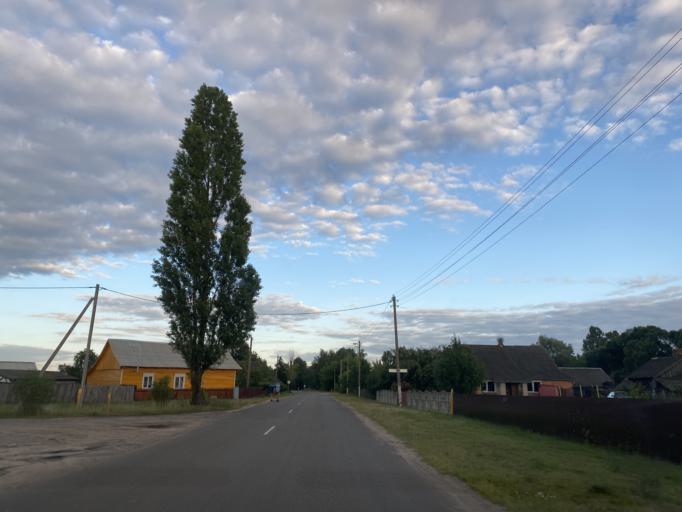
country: BY
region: Brest
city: Ivanava
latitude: 52.3448
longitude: 25.6161
